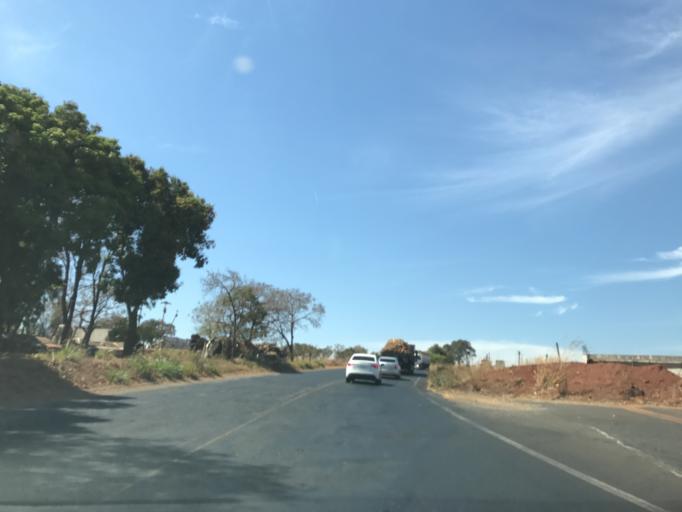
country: BR
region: Minas Gerais
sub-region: Monte Alegre De Minas
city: Monte Alegre de Minas
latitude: -18.8799
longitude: -49.0558
